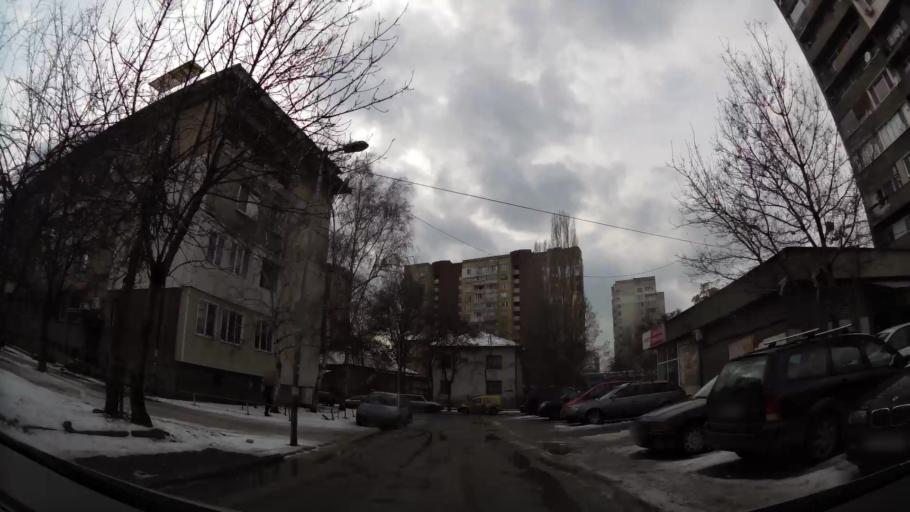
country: BG
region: Sofia-Capital
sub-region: Stolichna Obshtina
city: Sofia
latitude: 42.7032
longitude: 23.3658
